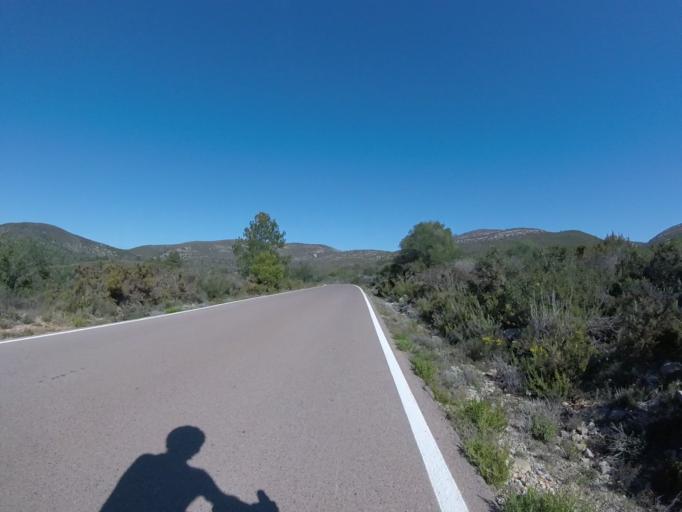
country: ES
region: Valencia
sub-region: Provincia de Castello
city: Santa Magdalena de Pulpis
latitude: 40.3763
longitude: 0.2716
